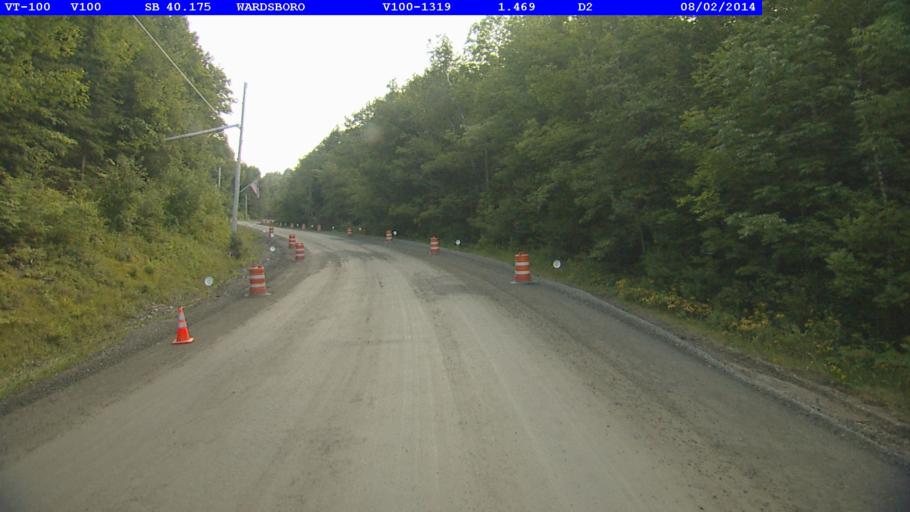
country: US
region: Vermont
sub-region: Windham County
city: Dover
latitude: 43.0195
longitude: -72.8569
